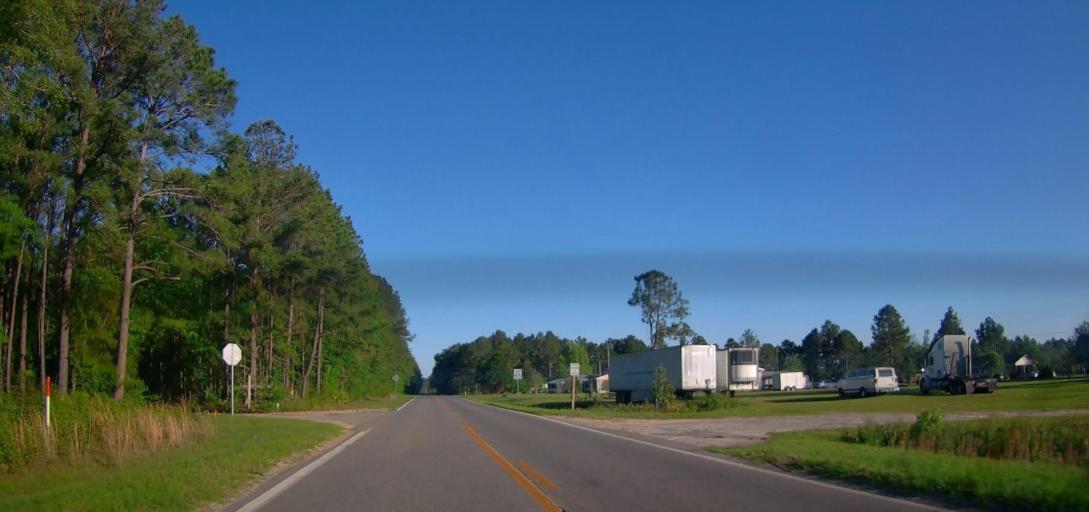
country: US
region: Georgia
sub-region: Ben Hill County
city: Fitzgerald
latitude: 31.6920
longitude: -83.2175
